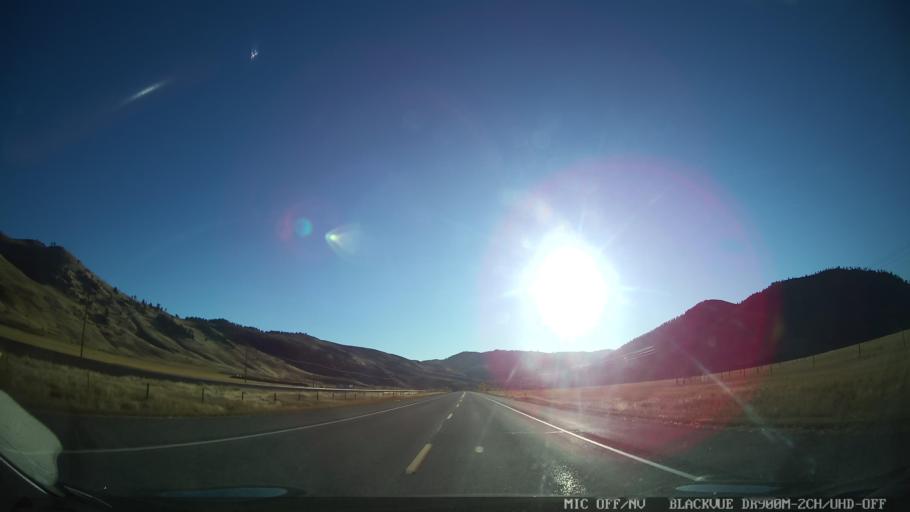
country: US
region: Colorado
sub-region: Grand County
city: Hot Sulphur Springs
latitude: 40.0513
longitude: -106.1465
